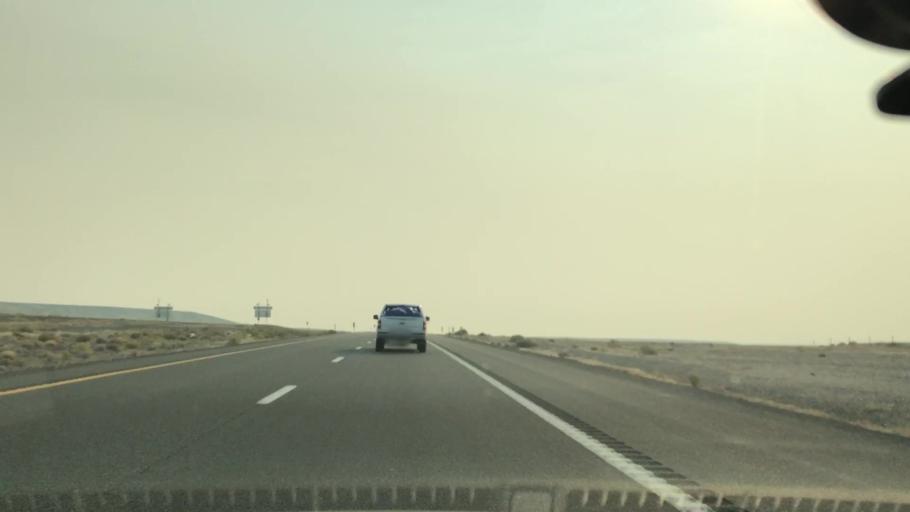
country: US
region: Nevada
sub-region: Pershing County
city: Lovelock
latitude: 39.9545
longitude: -118.7175
